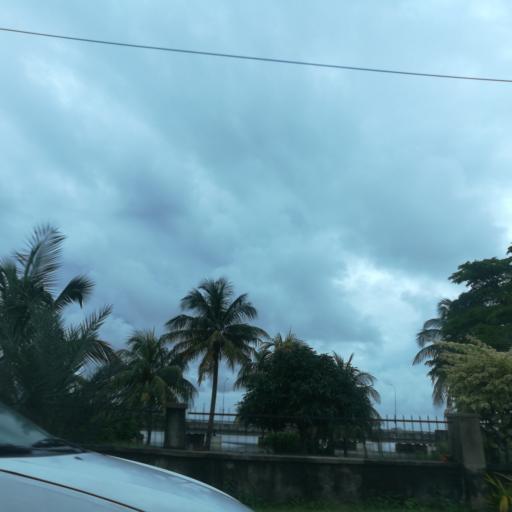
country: NG
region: Lagos
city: Ikoyi
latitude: 6.4471
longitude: 3.4594
